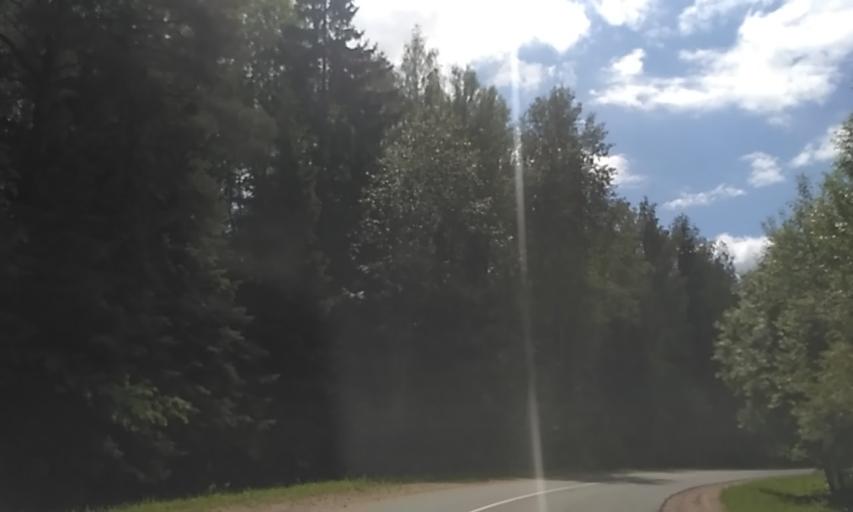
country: BY
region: Minsk
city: Khalopyenichy
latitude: 54.5181
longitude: 29.0755
